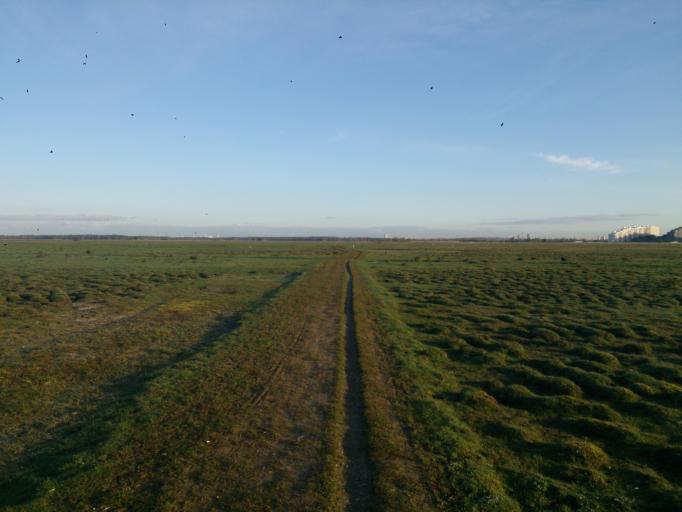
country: DK
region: Capital Region
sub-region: Tarnby Kommune
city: Tarnby
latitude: 55.6043
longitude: 12.5724
